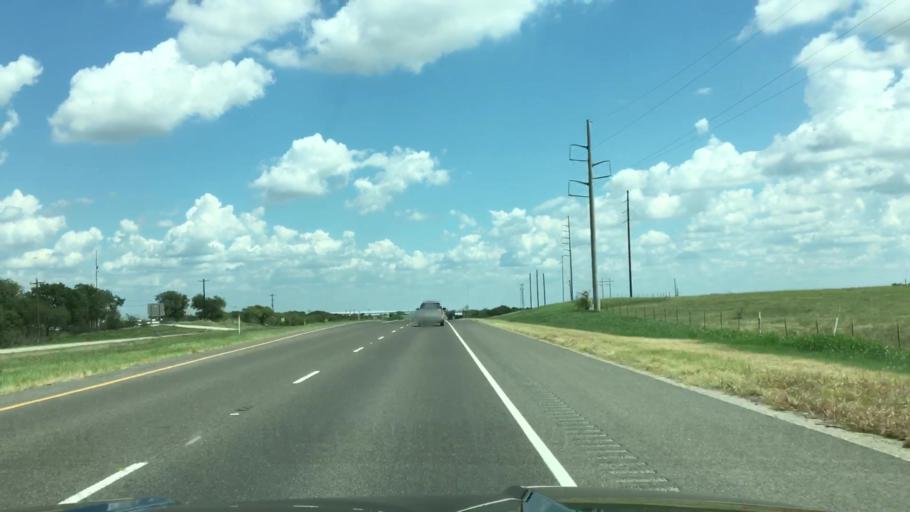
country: US
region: Texas
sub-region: Wise County
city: Rhome
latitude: 33.0366
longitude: -97.4129
